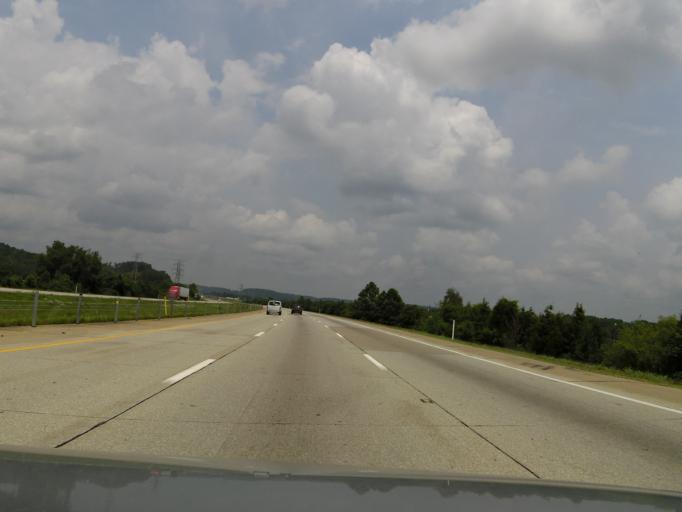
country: US
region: Kentucky
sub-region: Bullitt County
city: Shepherdsville
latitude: 37.9138
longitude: -85.6874
